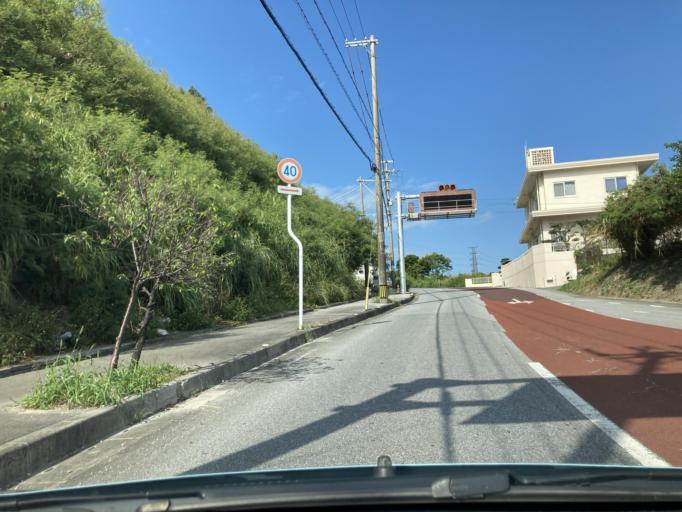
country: JP
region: Okinawa
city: Ginowan
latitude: 26.2736
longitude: 127.7968
